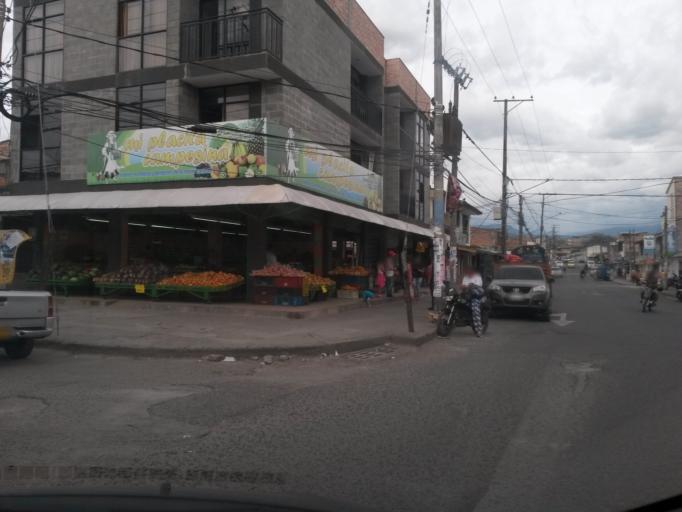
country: CO
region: Cauca
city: Popayan
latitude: 2.4438
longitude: -76.6187
